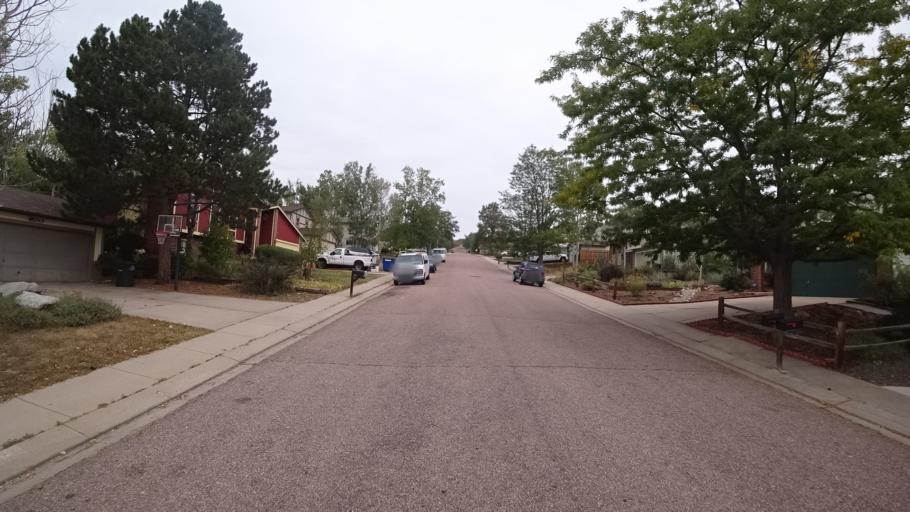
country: US
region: Colorado
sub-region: El Paso County
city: Cimarron Hills
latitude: 38.9044
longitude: -104.7336
